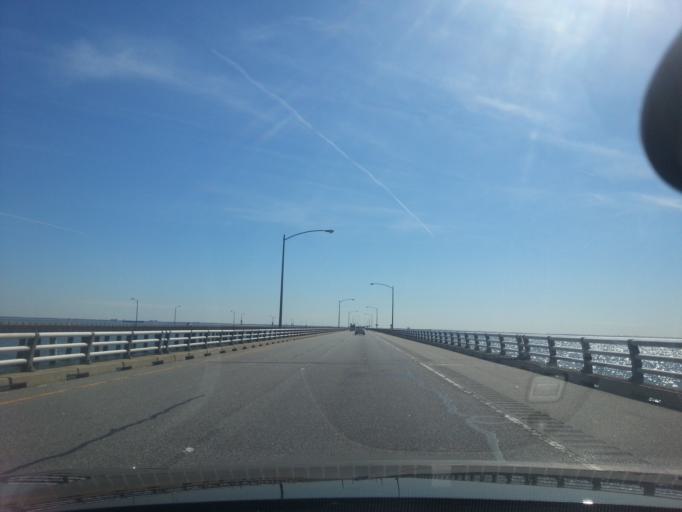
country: US
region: Virginia
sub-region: City of Virginia Beach
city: Virginia Beach
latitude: 37.0170
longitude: -76.0926
